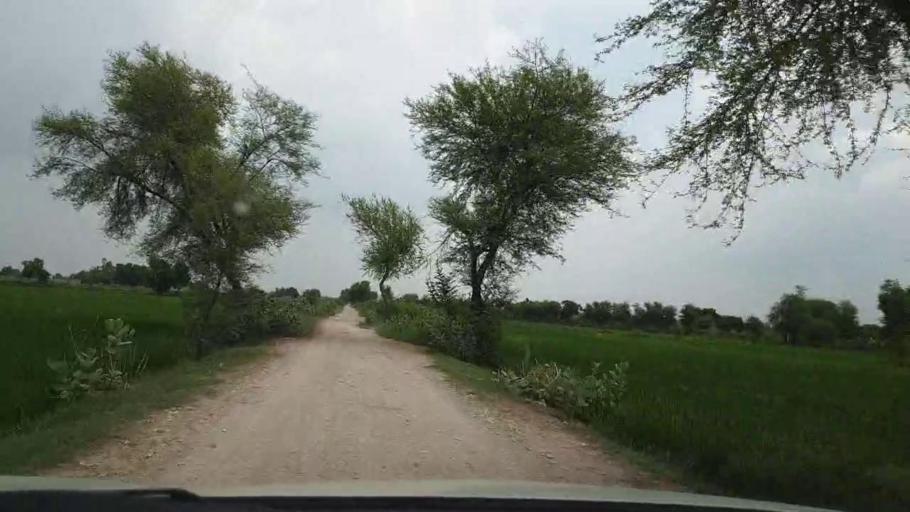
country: PK
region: Sindh
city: Goth Garelo
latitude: 27.4284
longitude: 68.0839
